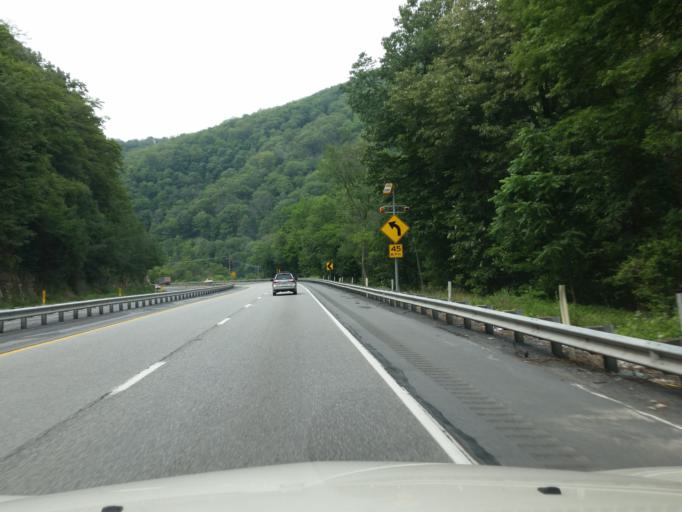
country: US
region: Pennsylvania
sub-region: Mifflin County
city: Yeagertown
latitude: 40.6513
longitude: -77.5829
